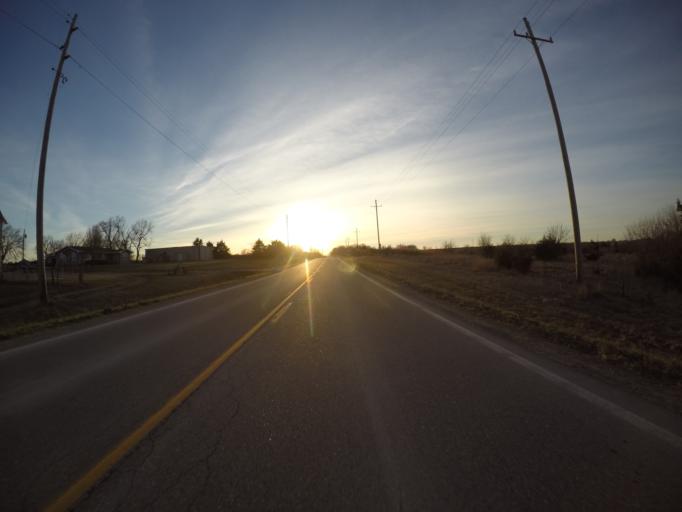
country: US
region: Kansas
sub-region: Riley County
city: Fort Riley North
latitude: 39.3645
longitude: -96.8469
